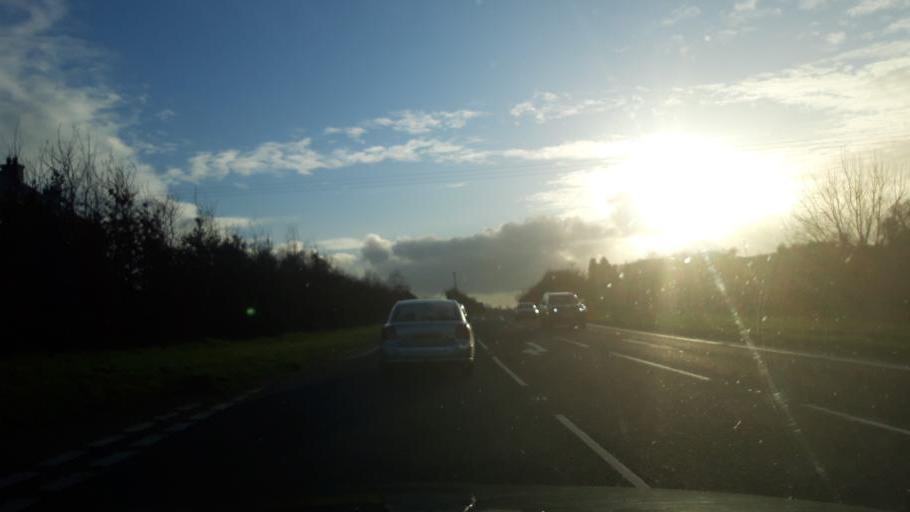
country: GB
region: Northern Ireland
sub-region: Dungannon District
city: Dungannon
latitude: 54.5411
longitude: -6.7780
